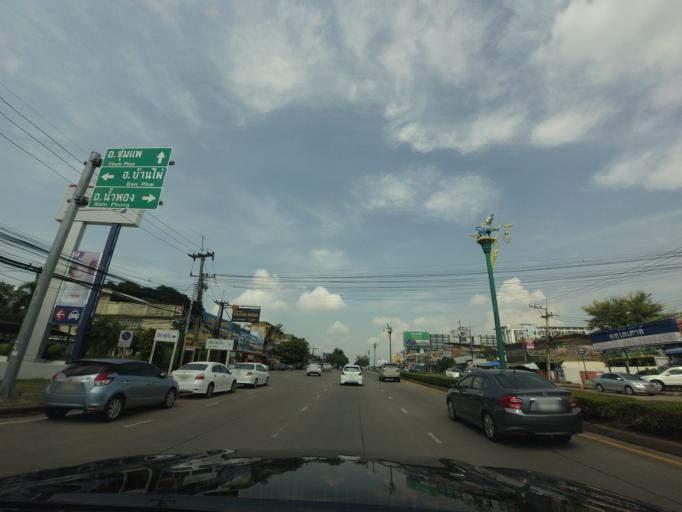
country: TH
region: Khon Kaen
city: Khon Kaen
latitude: 16.4402
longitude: 102.8237
